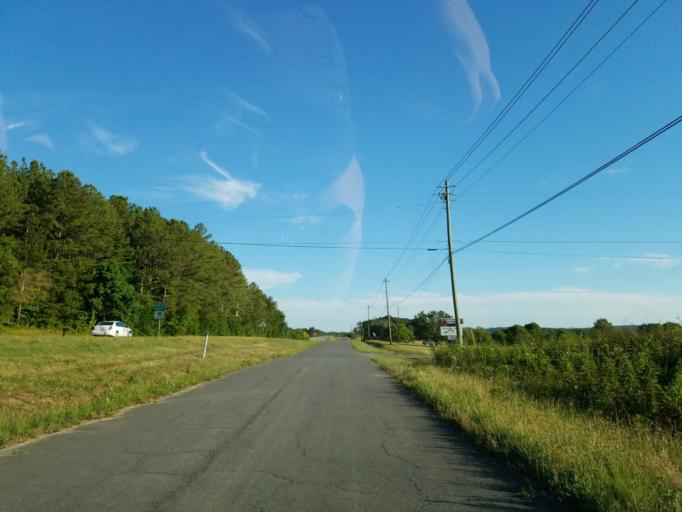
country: US
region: Georgia
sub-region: Bartow County
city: Adairsville
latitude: 34.3990
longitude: -84.9348
